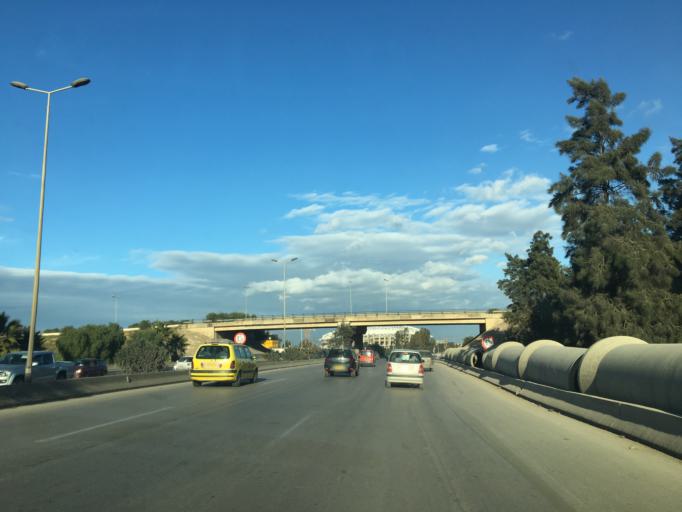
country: DZ
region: Tipaza
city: Baraki
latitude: 36.6860
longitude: 3.1133
